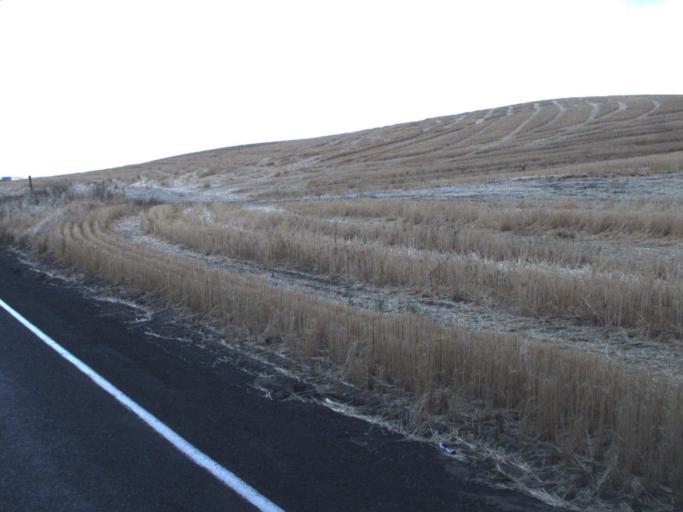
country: US
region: Washington
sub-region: Spokane County
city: Medical Lake
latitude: 47.5200
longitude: -117.9266
